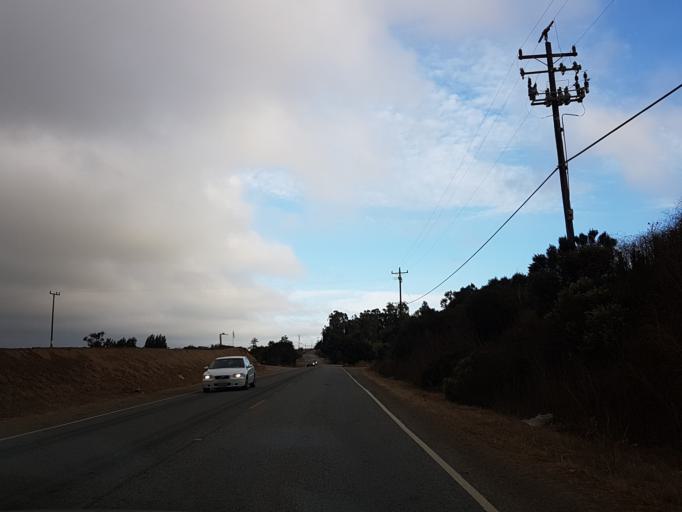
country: US
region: California
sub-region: Monterey County
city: Salinas
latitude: 36.5948
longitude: -121.6174
